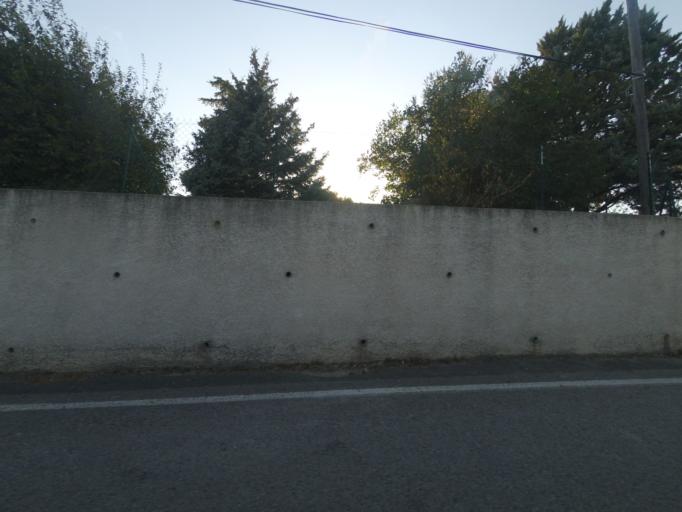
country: FR
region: Languedoc-Roussillon
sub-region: Departement du Gard
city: Calvisson
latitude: 43.7804
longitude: 4.1924
